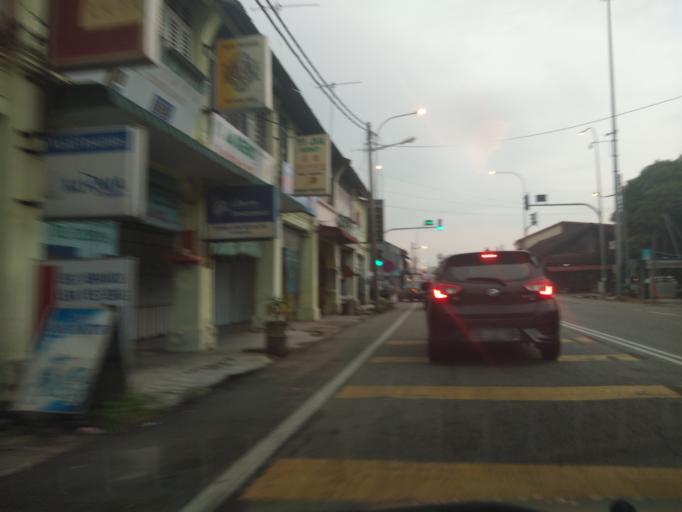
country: MY
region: Penang
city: Permatang Kuching
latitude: 5.4483
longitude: 100.3963
